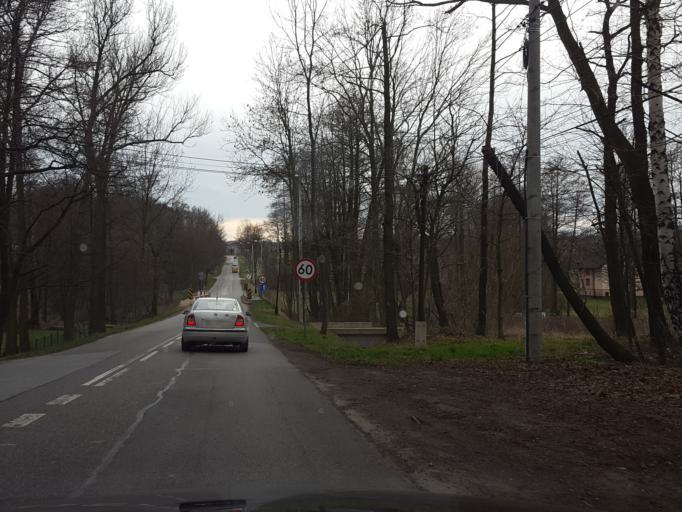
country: PL
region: Silesian Voivodeship
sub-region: Powiat gliwicki
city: Paniowki
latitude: 50.2070
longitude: 18.8114
